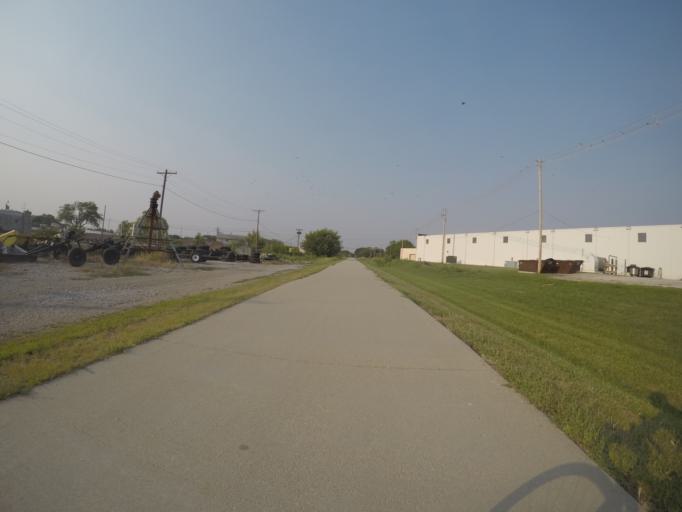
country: US
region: Nebraska
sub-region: Gage County
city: Beatrice
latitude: 40.2824
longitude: -96.7455
